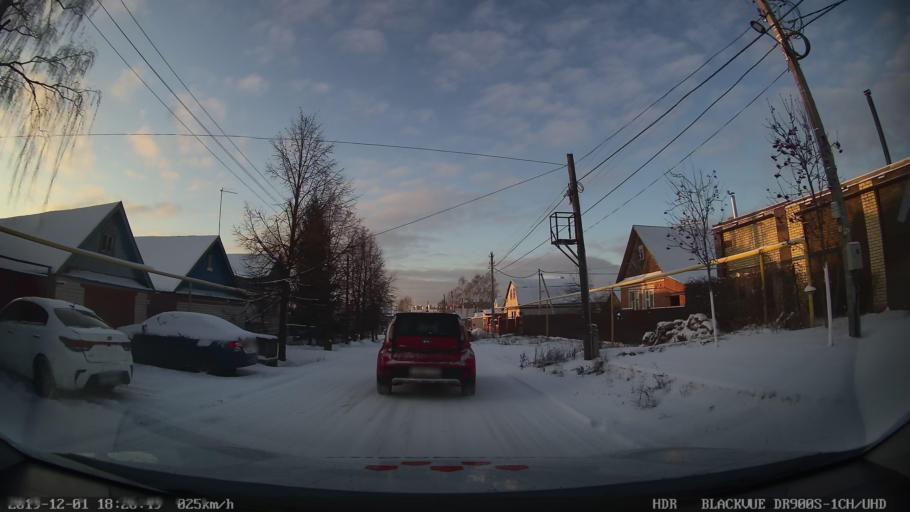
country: RU
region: Tatarstan
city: Vysokaya Gora
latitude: 55.8063
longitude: 49.2558
